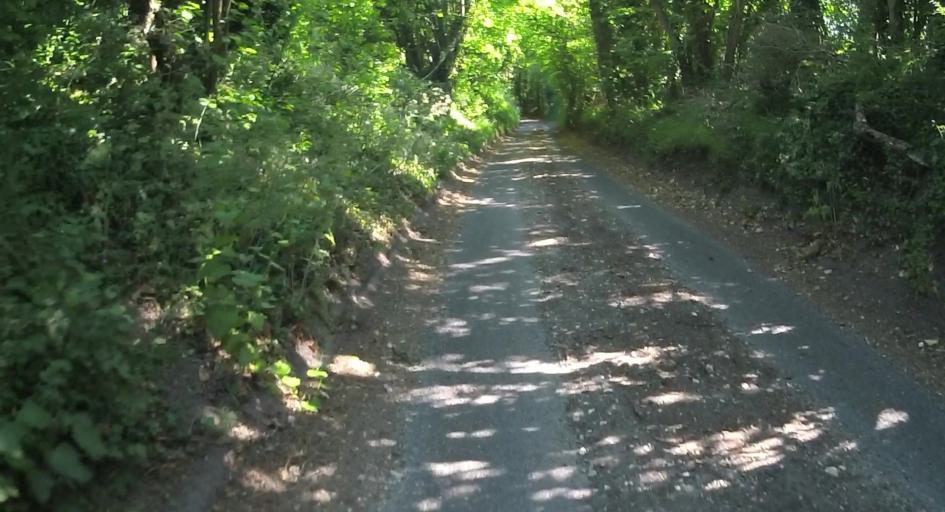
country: GB
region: England
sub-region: Hampshire
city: Old Basing
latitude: 51.2316
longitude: -1.0277
